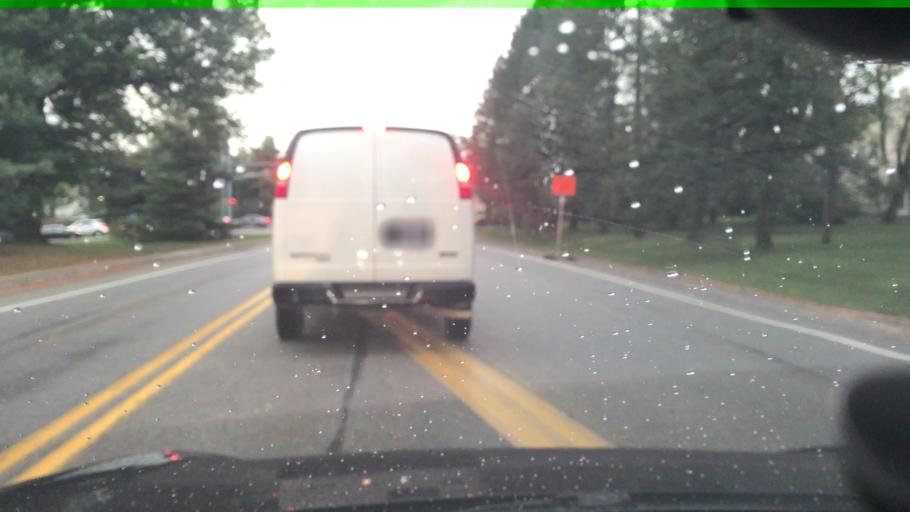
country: US
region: Pennsylvania
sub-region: Cumberland County
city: Shiremanstown
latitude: 40.2058
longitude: -76.9369
